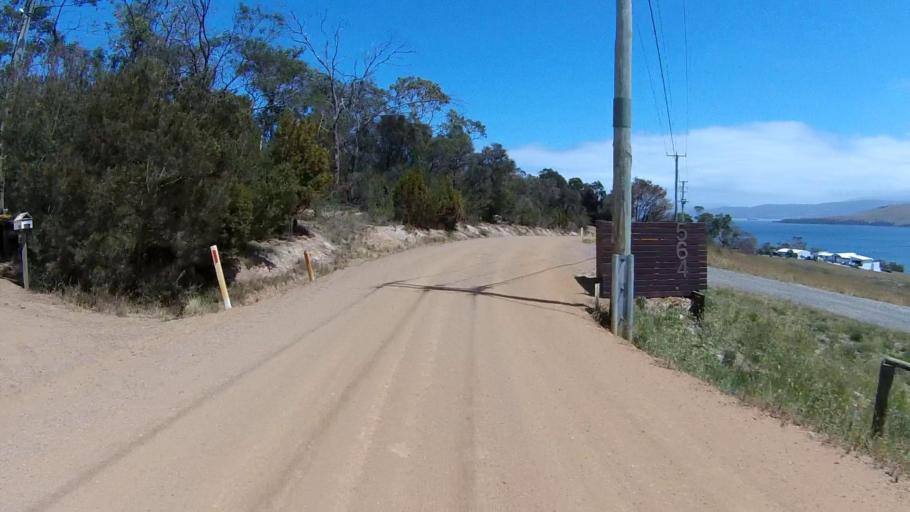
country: AU
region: Tasmania
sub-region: Clarence
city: Lauderdale
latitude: -42.9335
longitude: 147.4654
